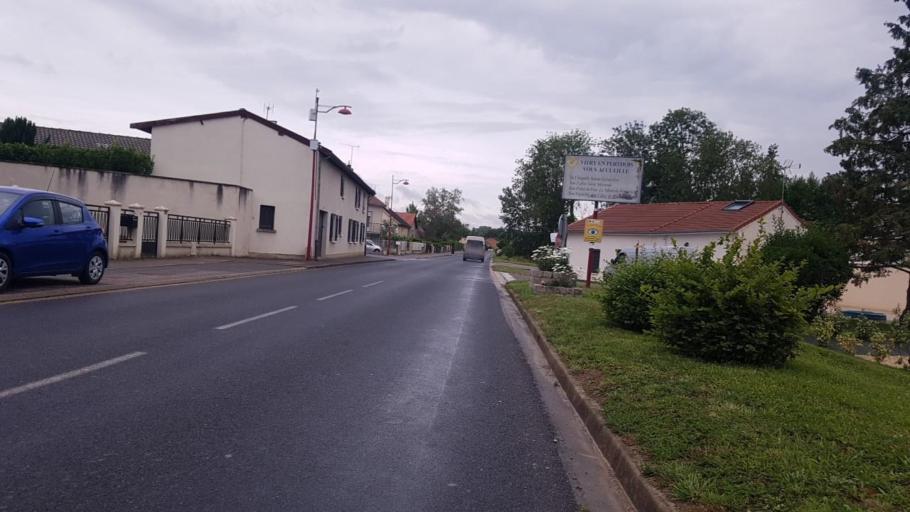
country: FR
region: Champagne-Ardenne
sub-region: Departement de la Marne
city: Vitry-le-Francois
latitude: 48.7413
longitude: 4.6356
